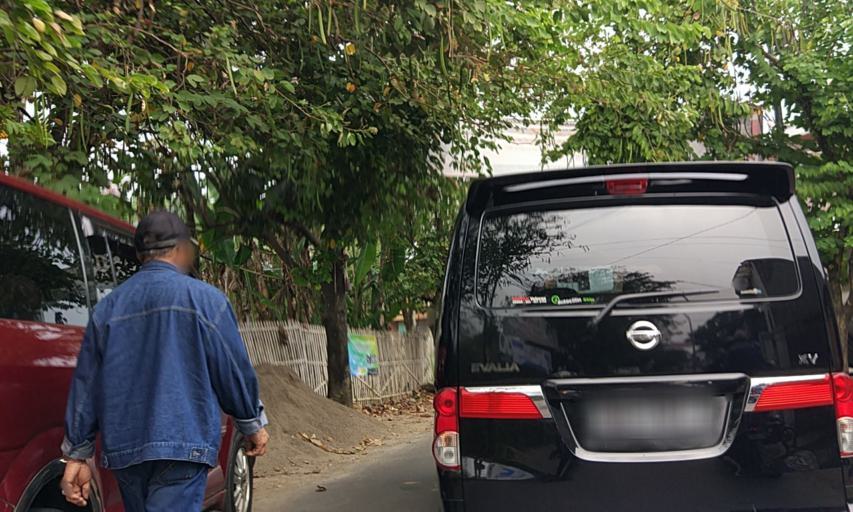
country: ID
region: West Java
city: Bandung
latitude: -6.9092
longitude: 107.6577
